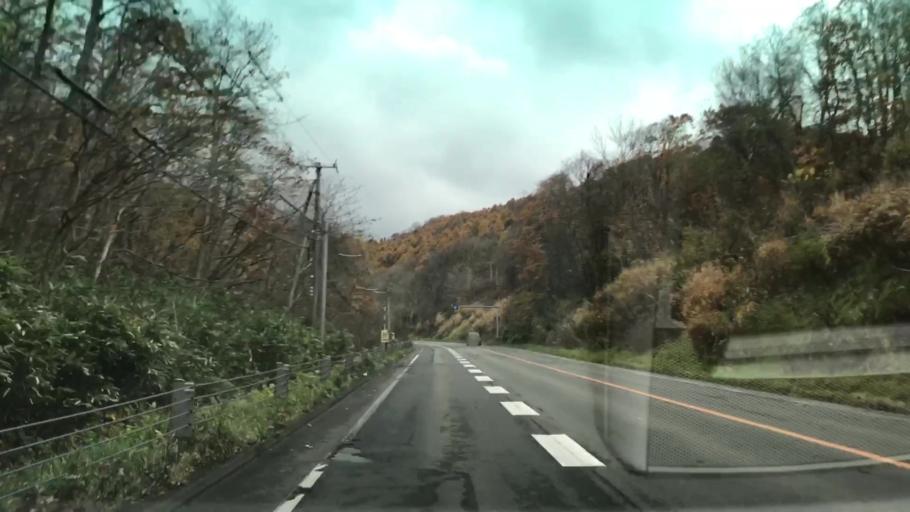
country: JP
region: Hokkaido
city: Yoichi
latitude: 43.2262
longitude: 140.7345
